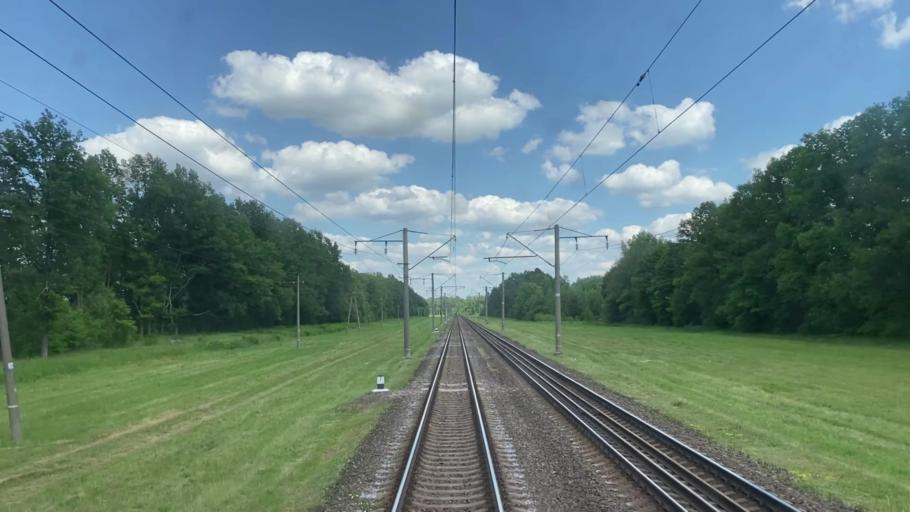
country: BY
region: Brest
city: Zhabinka
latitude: 52.2678
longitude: 24.1492
